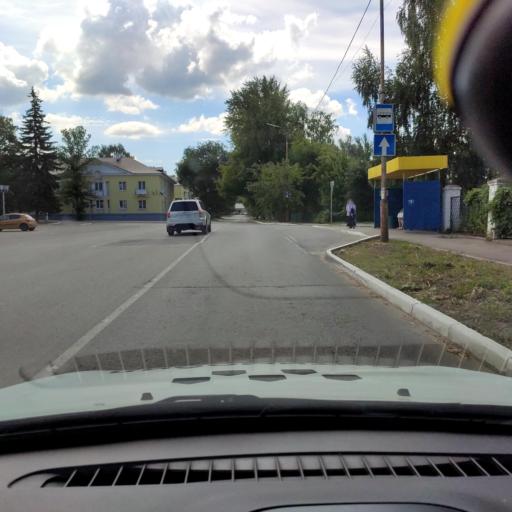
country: RU
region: Samara
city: Zhigulevsk
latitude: 53.4022
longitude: 49.4916
